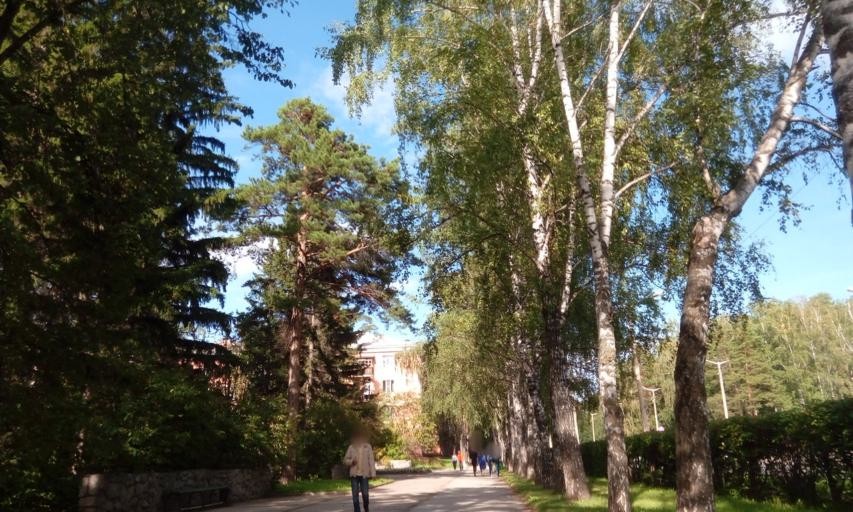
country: RU
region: Novosibirsk
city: Akademgorodok
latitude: 54.8365
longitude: 83.1007
